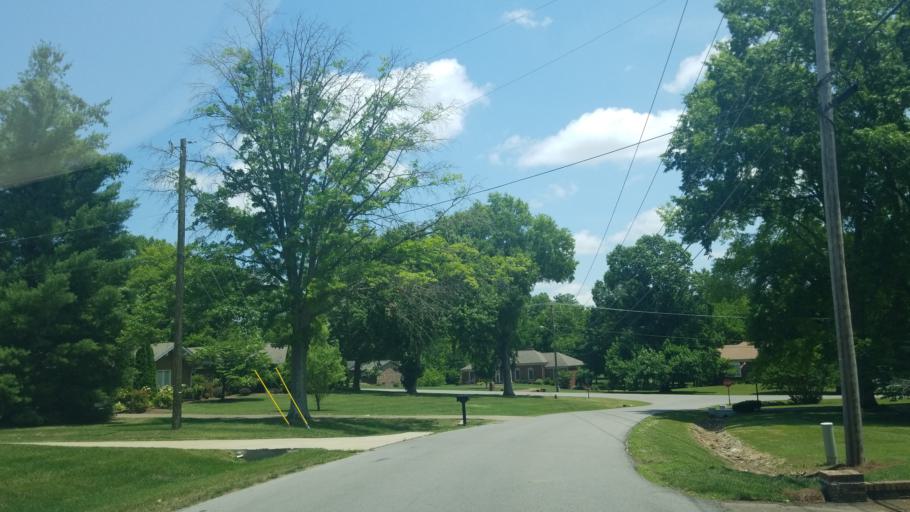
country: US
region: Tennessee
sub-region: Davidson County
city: Forest Hills
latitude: 36.0378
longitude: -86.8271
